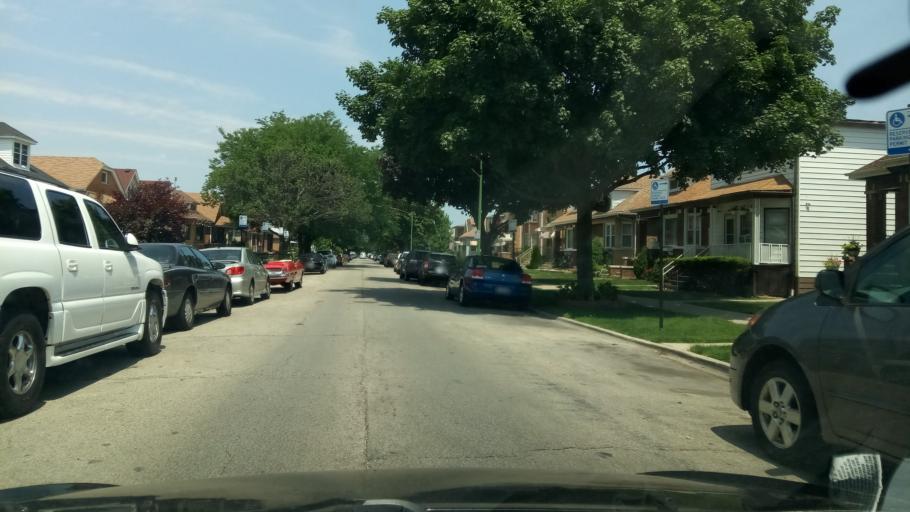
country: US
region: Illinois
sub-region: Cook County
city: Hometown
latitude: 41.7789
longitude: -87.7242
